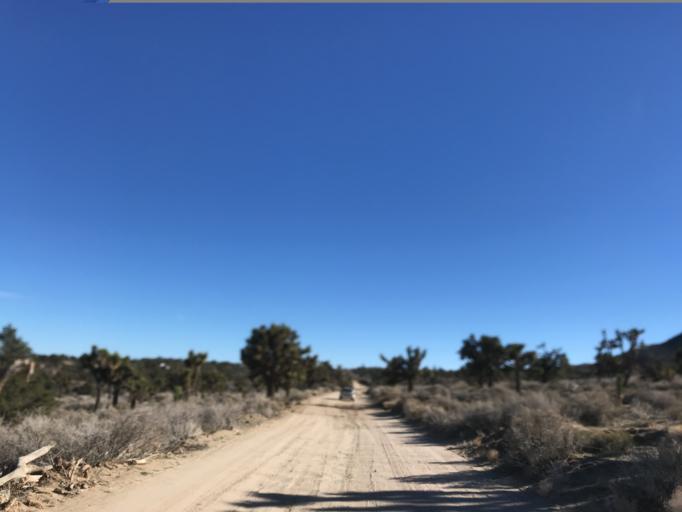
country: US
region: California
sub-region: San Bernardino County
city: Morongo Valley
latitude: 34.2177
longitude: -116.6177
